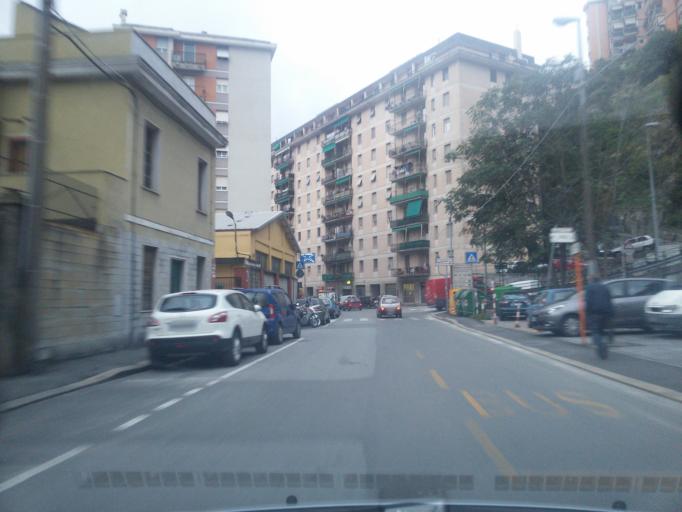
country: IT
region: Liguria
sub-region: Provincia di Genova
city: Piccarello
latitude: 44.4509
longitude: 8.9730
